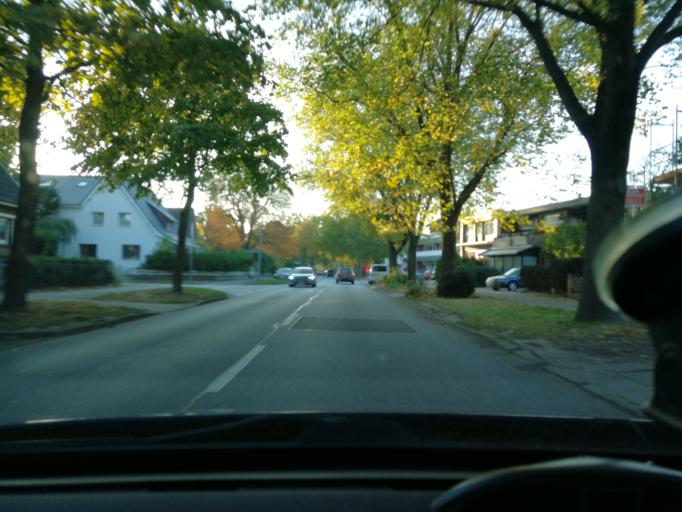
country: DE
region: Hamburg
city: Altona
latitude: 53.4779
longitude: 9.8901
